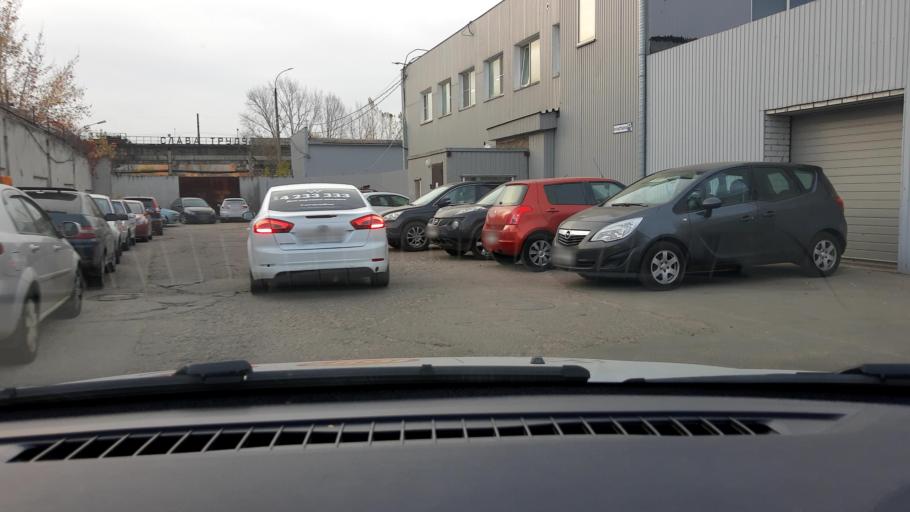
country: RU
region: Nizjnij Novgorod
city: Burevestnik
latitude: 56.2378
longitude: 43.8905
